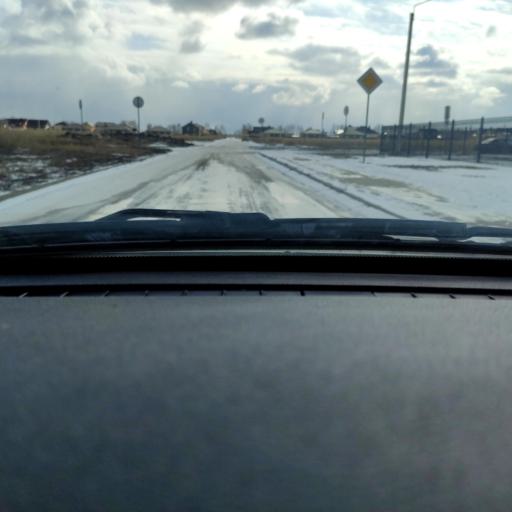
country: RU
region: Voronezj
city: Novaya Usman'
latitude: 51.6608
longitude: 39.4545
